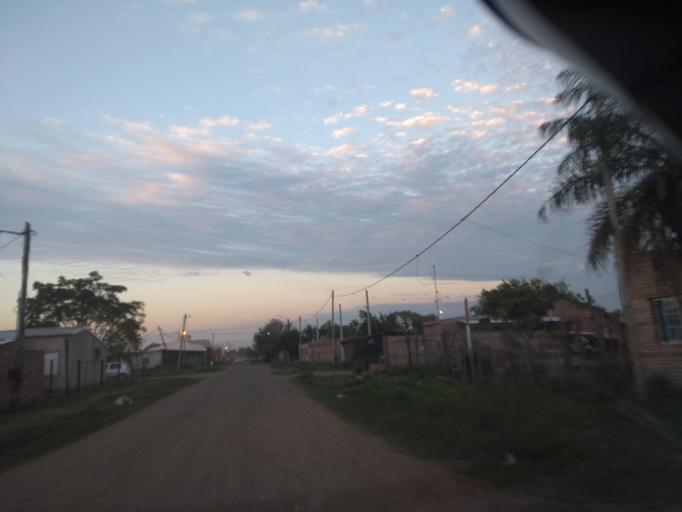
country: AR
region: Chaco
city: Fontana
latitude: -27.4051
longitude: -59.0461
